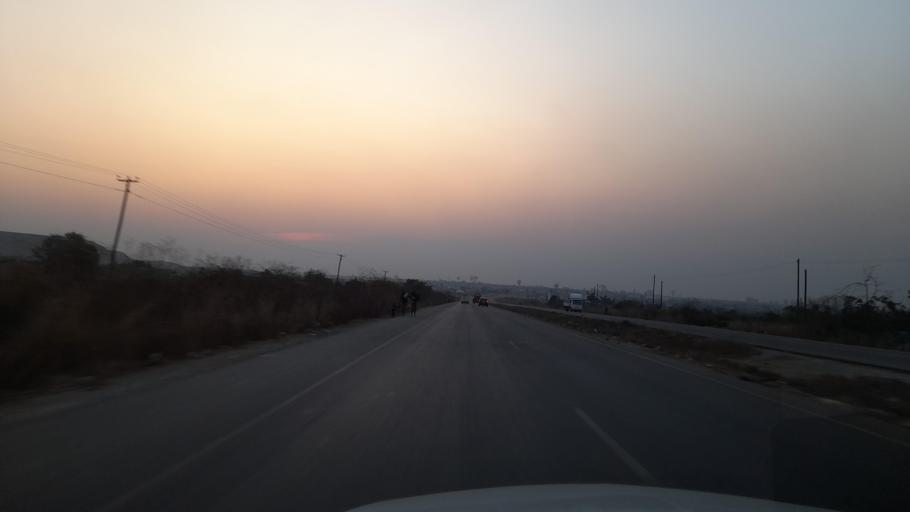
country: ZM
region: Copperbelt
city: Kitwe
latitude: -12.7666
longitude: 28.1759
